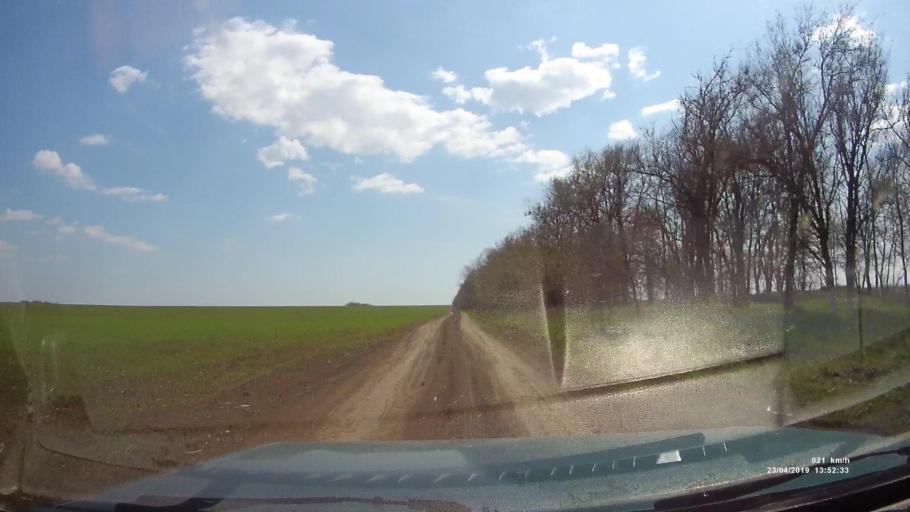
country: RU
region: Rostov
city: Remontnoye
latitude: 46.5992
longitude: 42.9525
